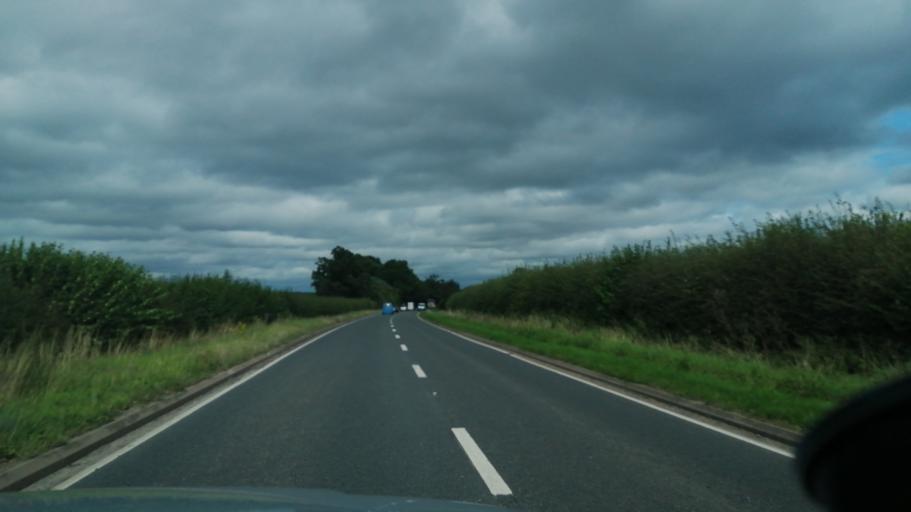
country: GB
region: Wales
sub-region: Monmouthshire
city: Grosmont
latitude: 51.9541
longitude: -2.8625
